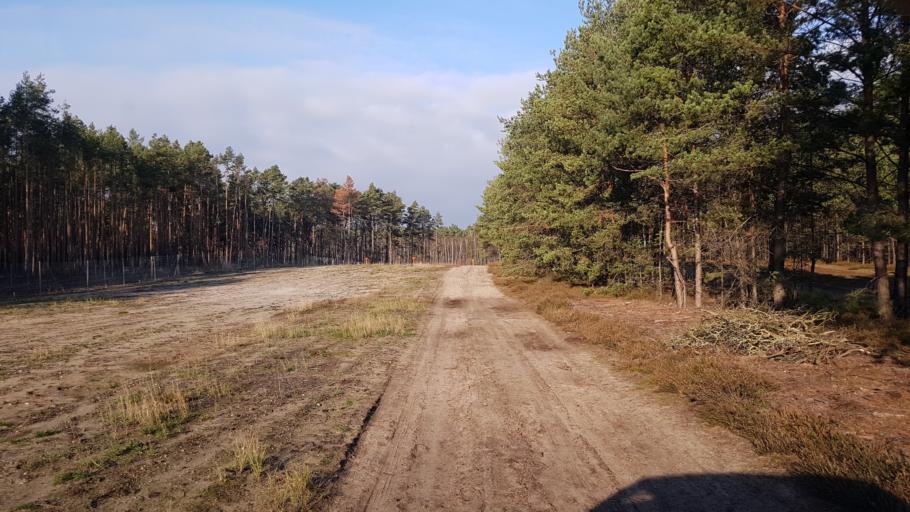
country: DE
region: Brandenburg
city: Finsterwalde
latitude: 51.6435
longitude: 13.6683
